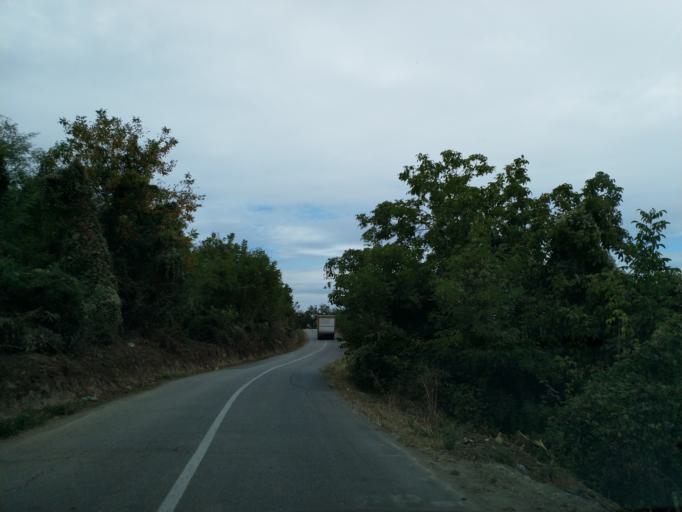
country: RS
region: Central Serbia
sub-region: Pomoravski Okrug
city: Cuprija
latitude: 43.8583
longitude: 21.3250
